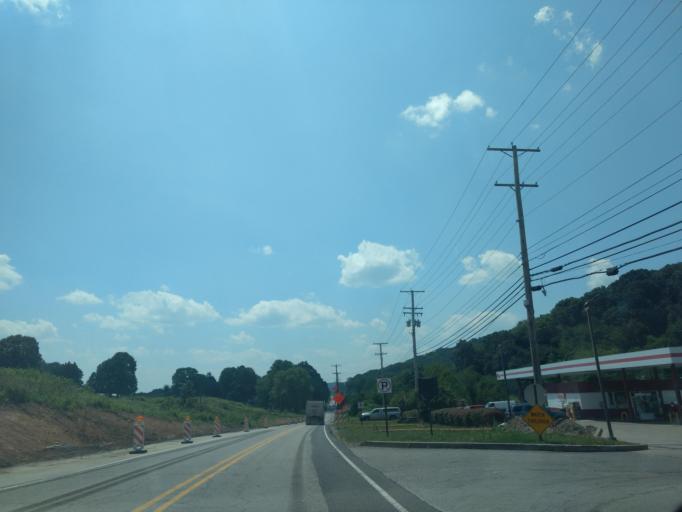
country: US
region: Pennsylvania
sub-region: Butler County
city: Zelienople
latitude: 40.8110
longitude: -80.1272
